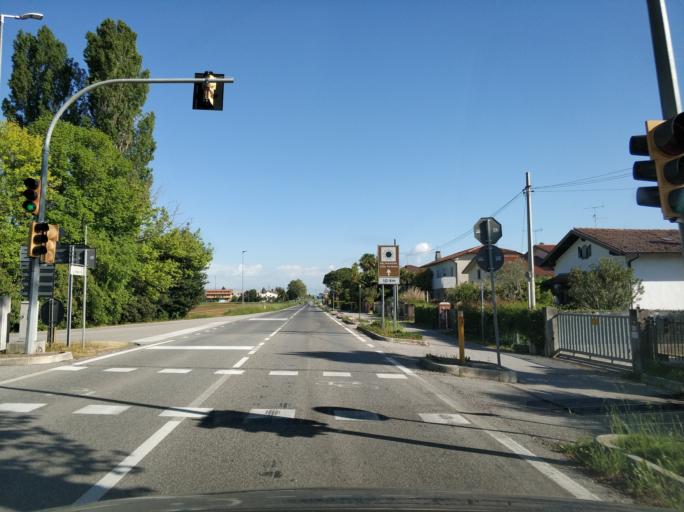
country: IT
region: Friuli Venezia Giulia
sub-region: Provincia di Udine
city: Terzo d'Aquileia
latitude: 45.8065
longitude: 13.3438
